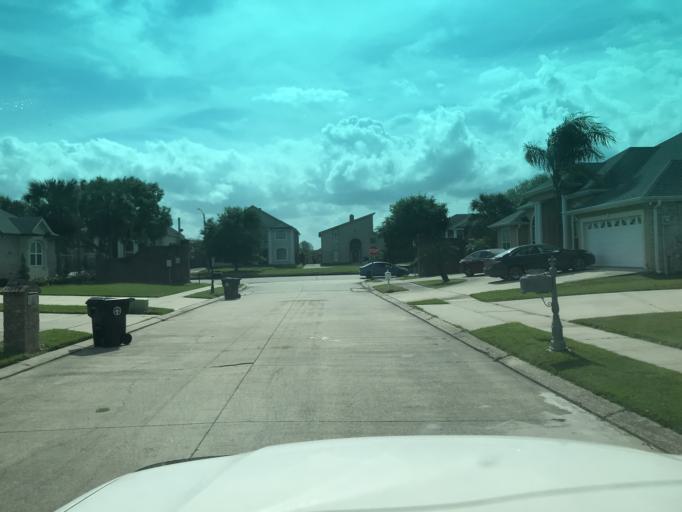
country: US
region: Louisiana
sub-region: Saint Bernard Parish
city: Chalmette
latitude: 30.0355
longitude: -89.9515
